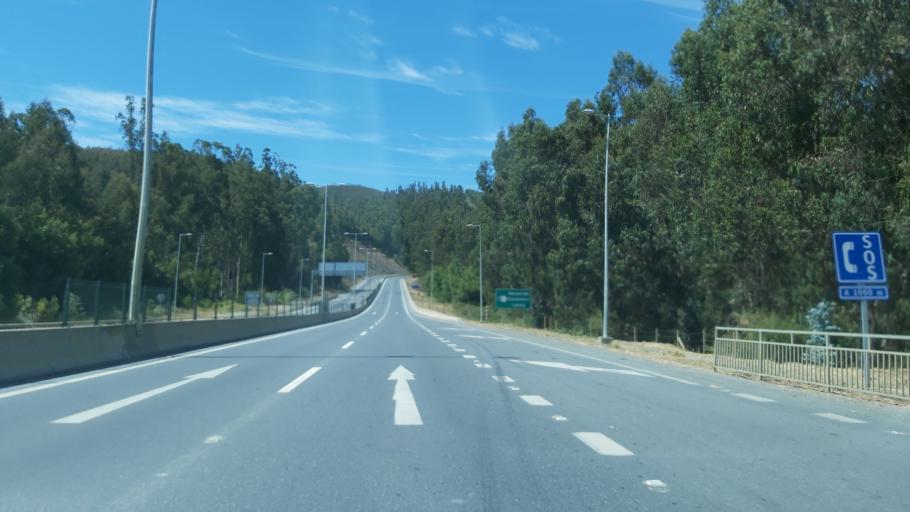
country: CL
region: Biobio
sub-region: Provincia de Concepcion
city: Lota
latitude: -37.1143
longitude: -73.1484
